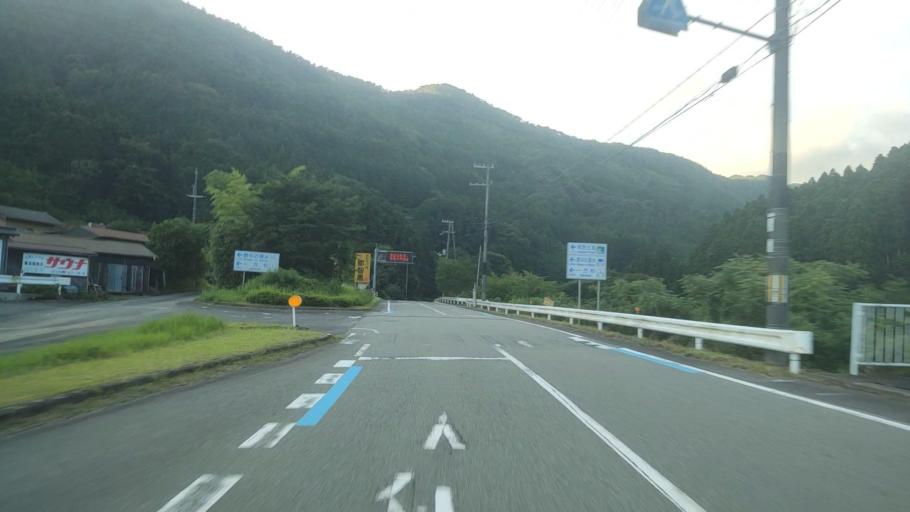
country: JP
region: Wakayama
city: Tanabe
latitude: 33.8232
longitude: 135.6313
